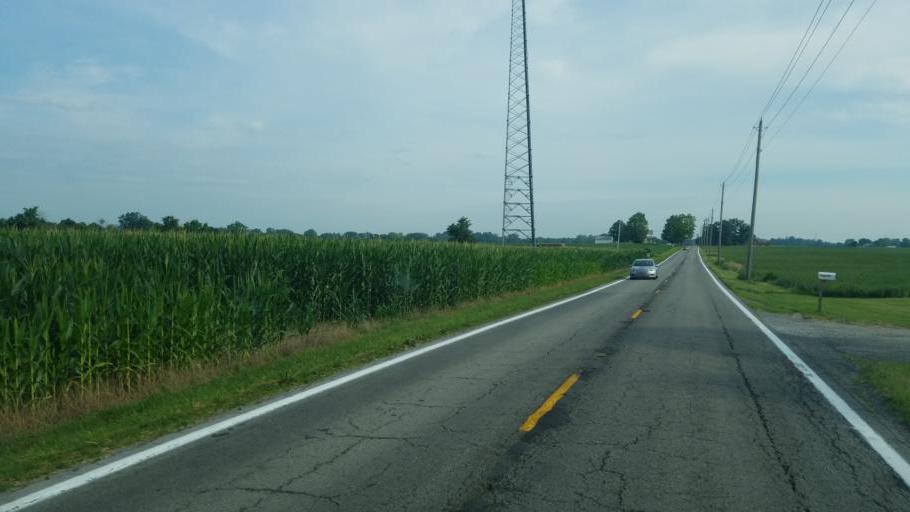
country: US
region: Ohio
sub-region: Marion County
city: Prospect
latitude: 40.5300
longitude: -83.1897
